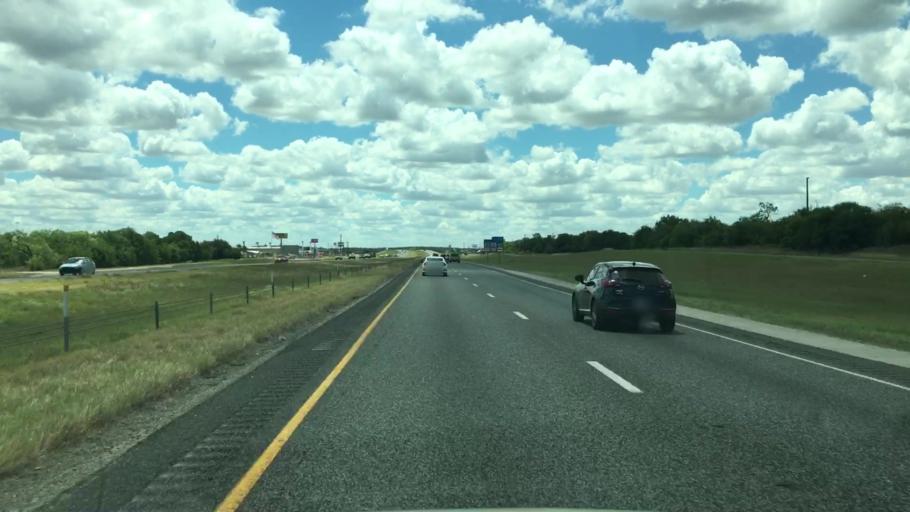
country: US
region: Texas
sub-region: Bexar County
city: Elmendorf
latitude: 29.2290
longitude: -98.4067
